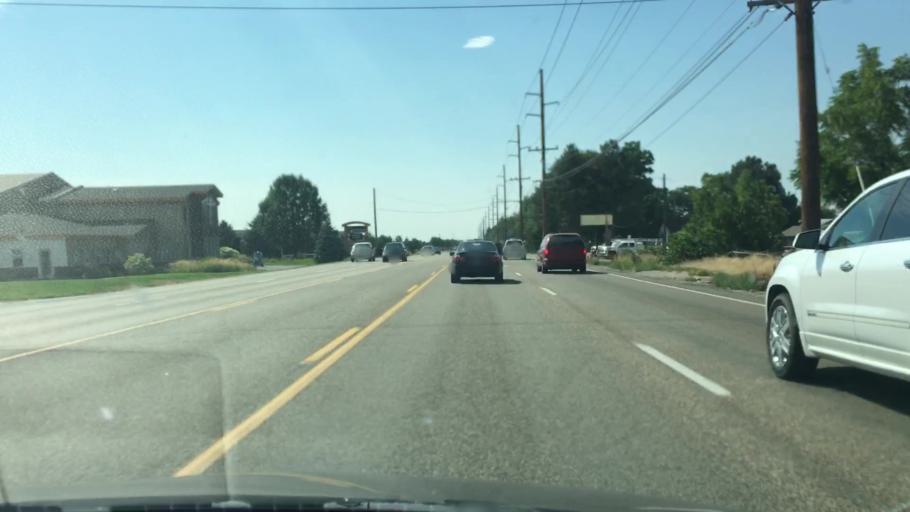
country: US
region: Idaho
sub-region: Ada County
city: Eagle
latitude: 43.6790
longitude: -116.3035
